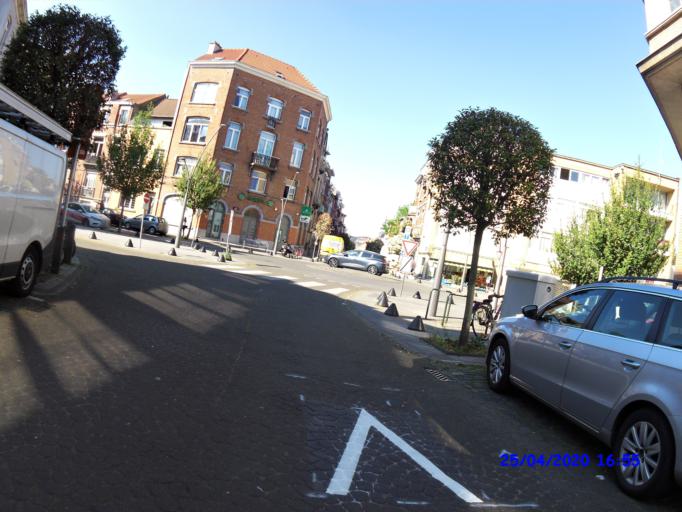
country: BE
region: Brussels Capital
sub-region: Bruxelles-Capitale
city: Brussels
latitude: 50.8769
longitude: 4.3265
